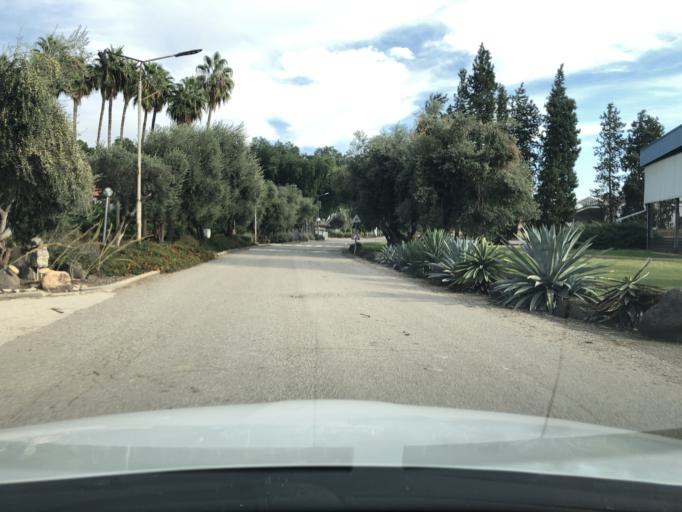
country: IL
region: Northern District
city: Yavne'el
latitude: 32.6581
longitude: 35.5788
